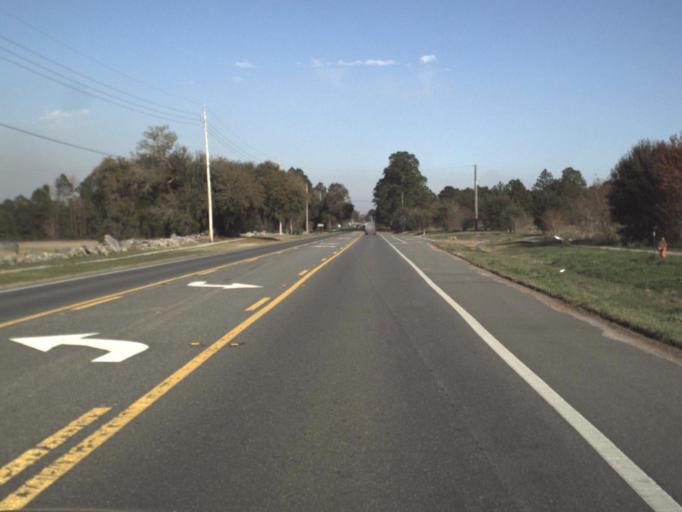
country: US
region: Florida
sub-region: Jackson County
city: Marianna
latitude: 30.8123
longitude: -85.1886
